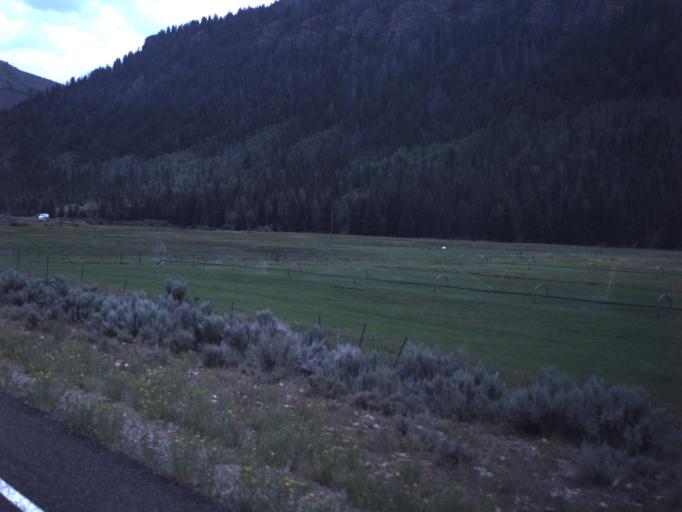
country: US
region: Utah
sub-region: Summit County
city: Francis
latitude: 40.4531
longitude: -110.8753
